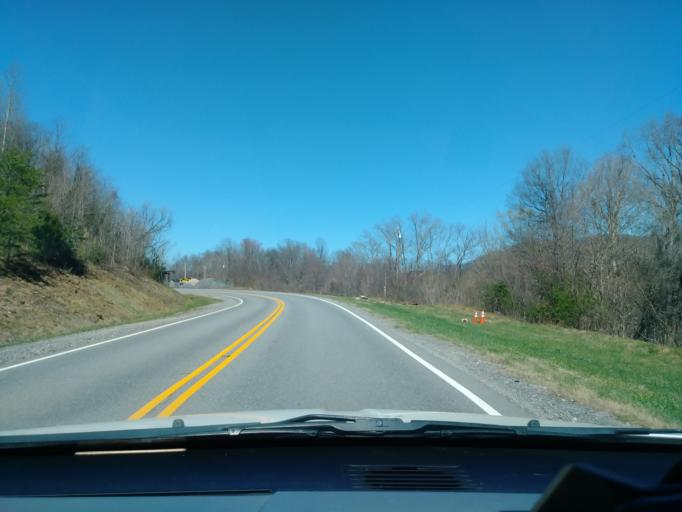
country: US
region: North Carolina
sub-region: Madison County
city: Marshall
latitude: 35.9003
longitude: -82.8457
